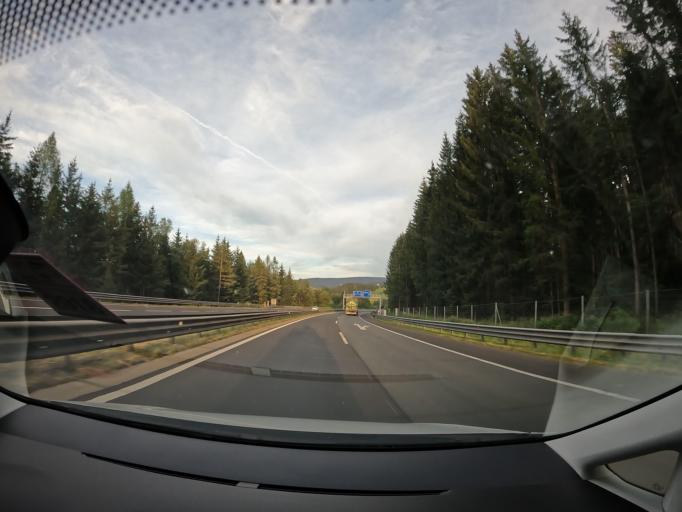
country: AT
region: Styria
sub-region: Politischer Bezirk Voitsberg
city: Modriach
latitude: 46.9570
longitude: 15.0386
